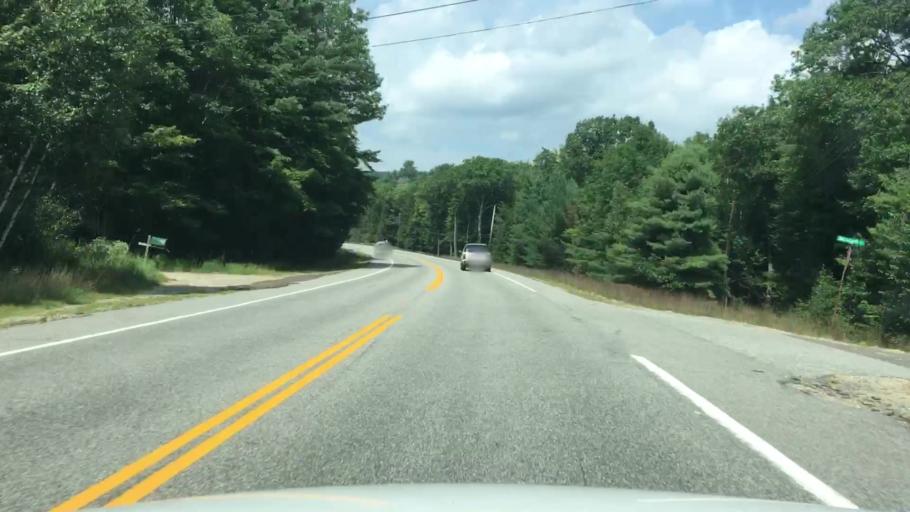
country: US
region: Maine
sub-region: Androscoggin County
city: Livermore
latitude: 44.3979
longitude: -70.2578
